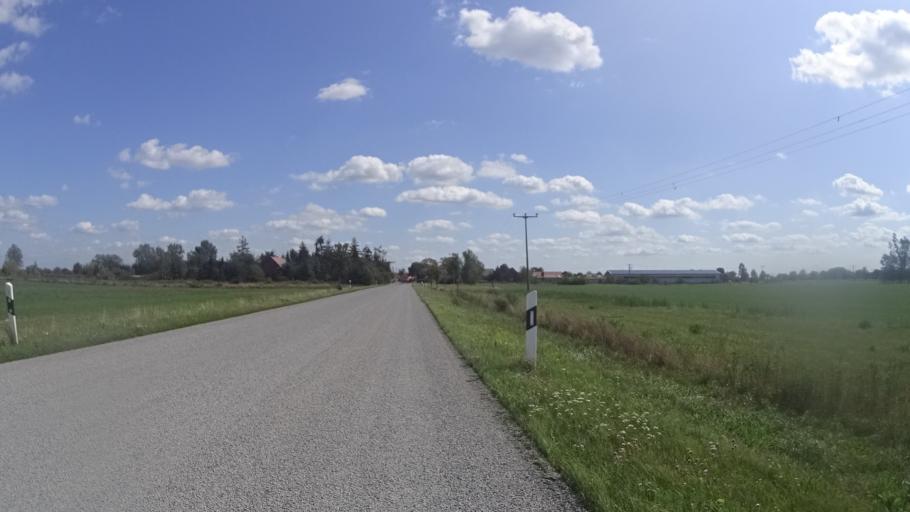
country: DE
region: Saxony-Anhalt
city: Kamern
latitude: 52.7862
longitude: 12.1887
